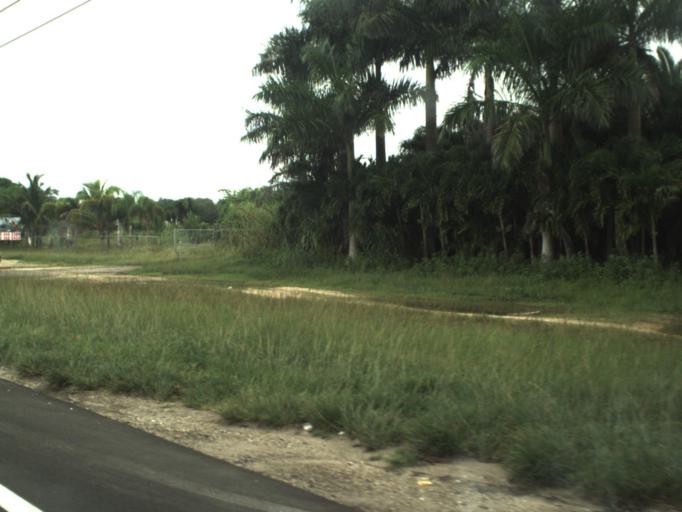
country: US
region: Florida
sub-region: Miami-Dade County
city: Country Walk
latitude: 25.6237
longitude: -80.4795
